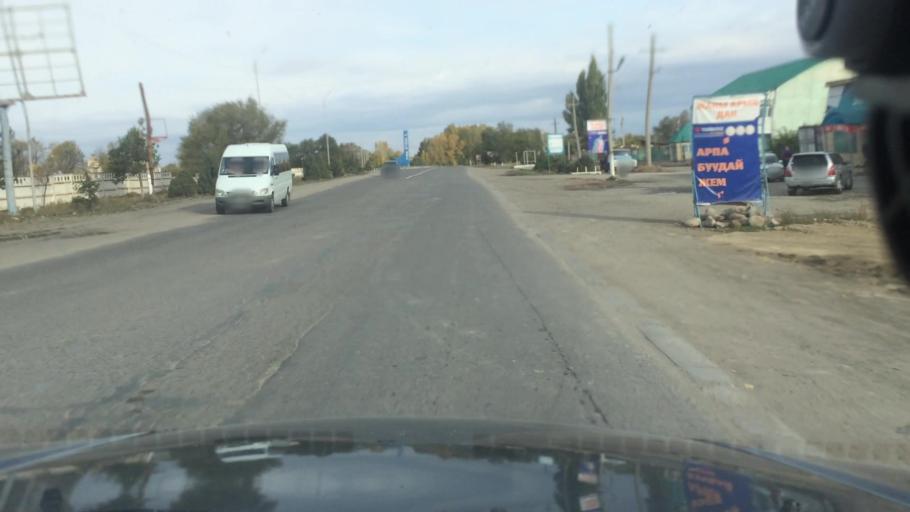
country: KG
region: Ysyk-Koel
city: Karakol
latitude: 42.5303
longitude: 78.3829
